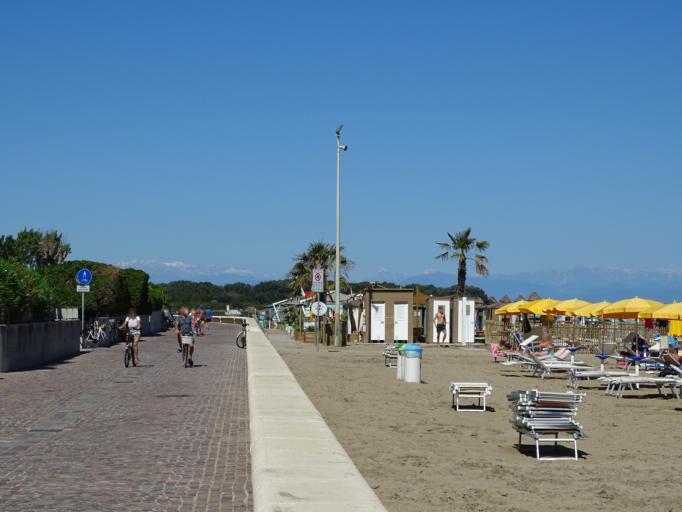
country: IT
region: Friuli Venezia Giulia
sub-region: Provincia di Udine
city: Lignano Sabbiadoro
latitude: 45.6945
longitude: 13.1519
